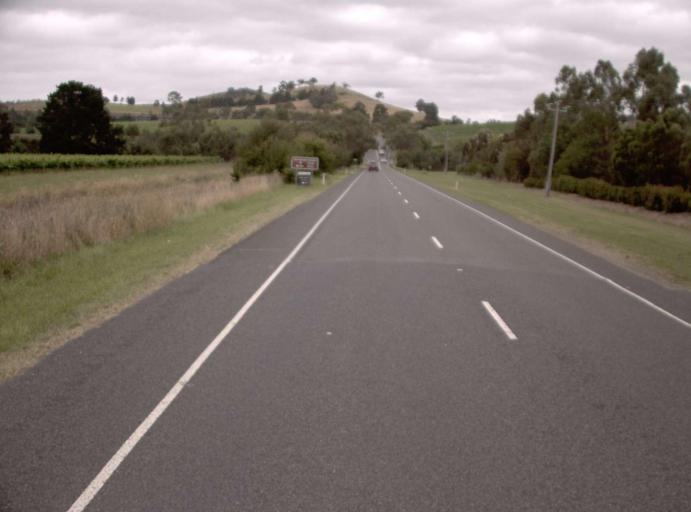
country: AU
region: Victoria
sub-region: Yarra Ranges
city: Yarra Glen
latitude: -37.6394
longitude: 145.3997
